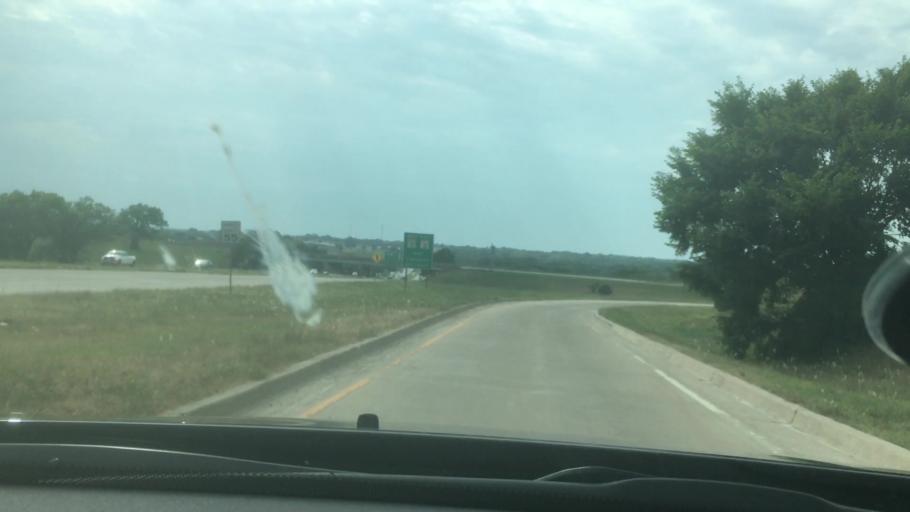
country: US
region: Oklahoma
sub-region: Pontotoc County
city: Ada
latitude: 34.7752
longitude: -96.6988
